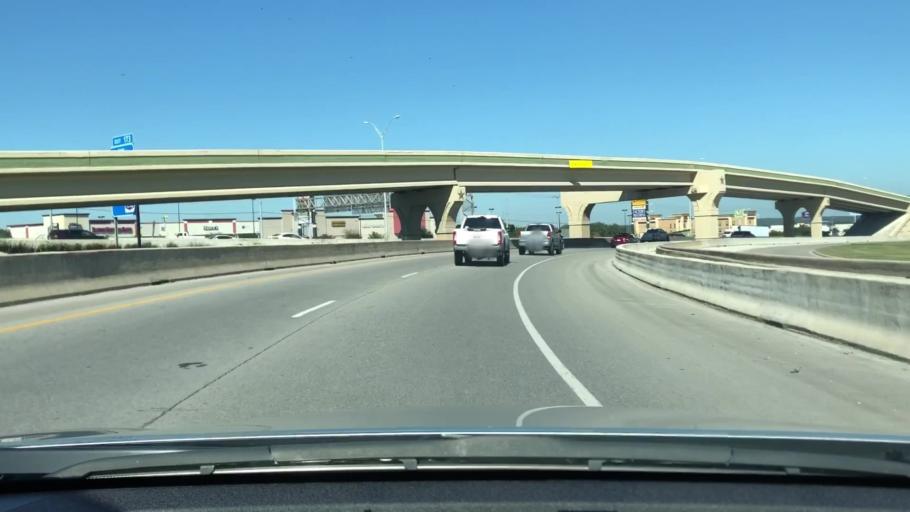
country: US
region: Texas
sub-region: Bexar County
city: Live Oak
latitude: 29.5688
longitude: -98.3312
